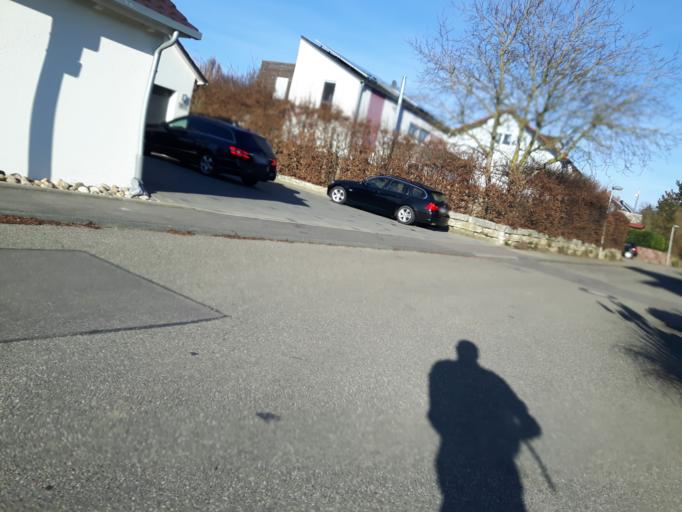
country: DE
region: Baden-Wuerttemberg
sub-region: Regierungsbezirk Stuttgart
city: Leingarten
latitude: 49.1510
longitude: 9.1003
